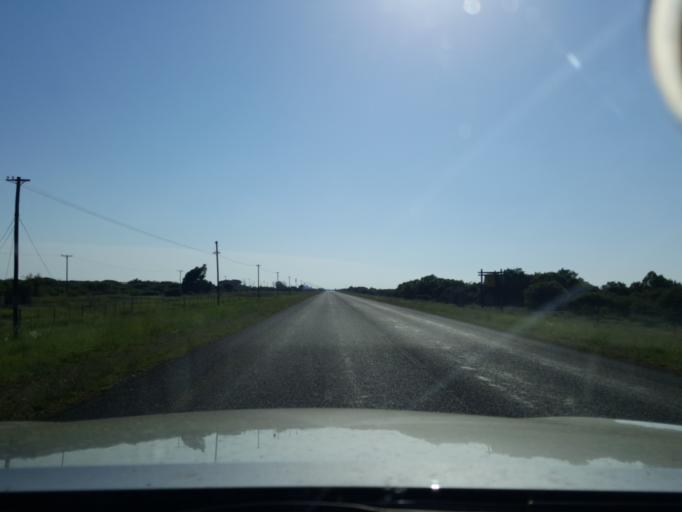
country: ZA
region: North-West
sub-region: Ngaka Modiri Molema District Municipality
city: Mahikeng
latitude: -25.8395
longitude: 25.7399
